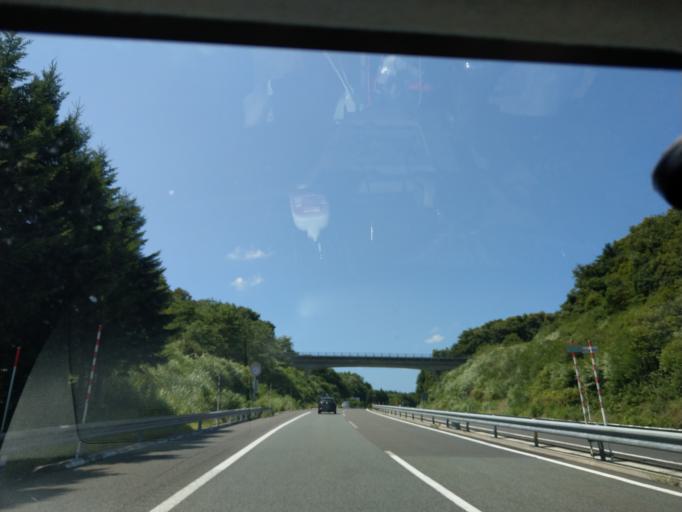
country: JP
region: Akita
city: Akita
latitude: 39.6007
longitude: 140.2687
